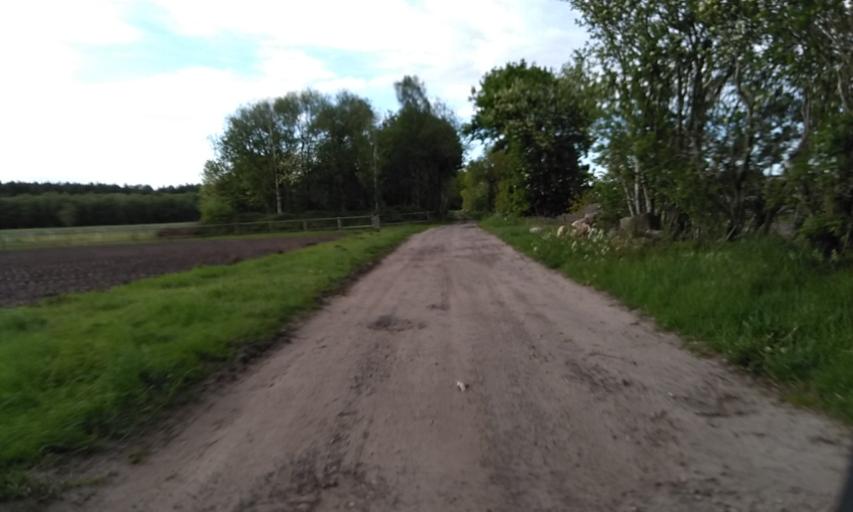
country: DE
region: Lower Saxony
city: Apensen
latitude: 53.4360
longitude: 9.5914
